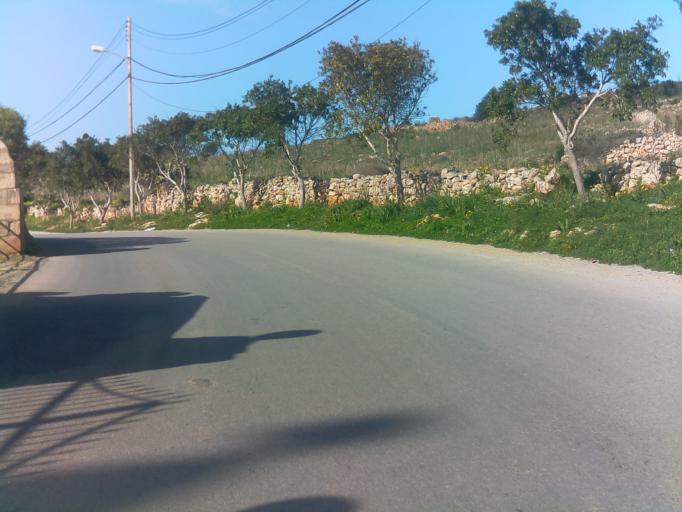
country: MT
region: L-Imgarr
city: Imgarr
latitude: 35.9211
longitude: 14.3595
